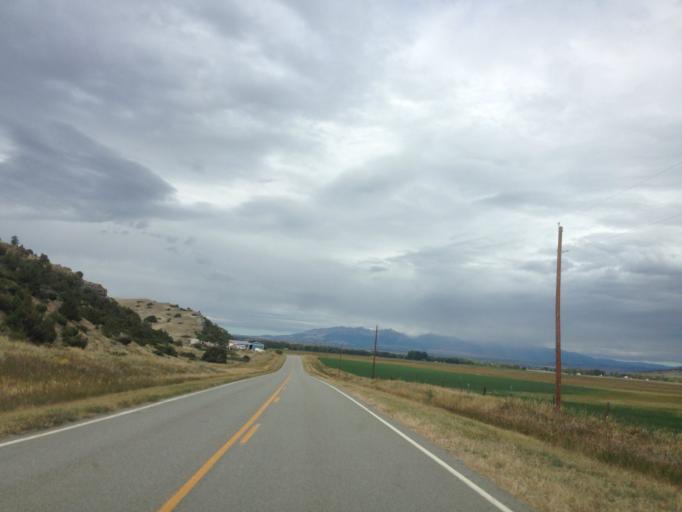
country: US
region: Montana
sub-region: Sweet Grass County
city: Big Timber
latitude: 45.7782
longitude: -109.8119
